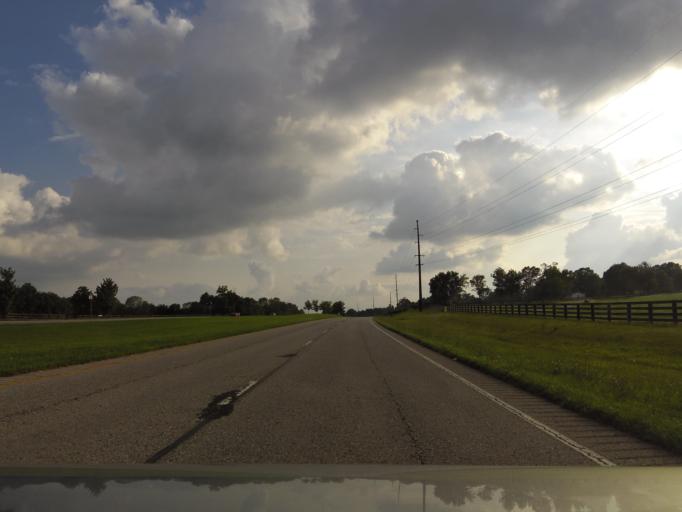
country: US
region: Kentucky
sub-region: Bourbon County
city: Paris
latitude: 38.1380
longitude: -84.3617
